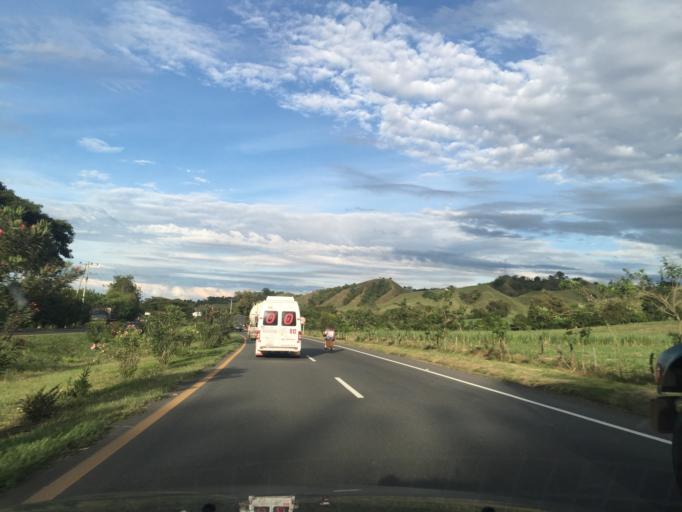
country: CO
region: Valle del Cauca
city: Bugalagrande
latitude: 4.2285
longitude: -76.1374
